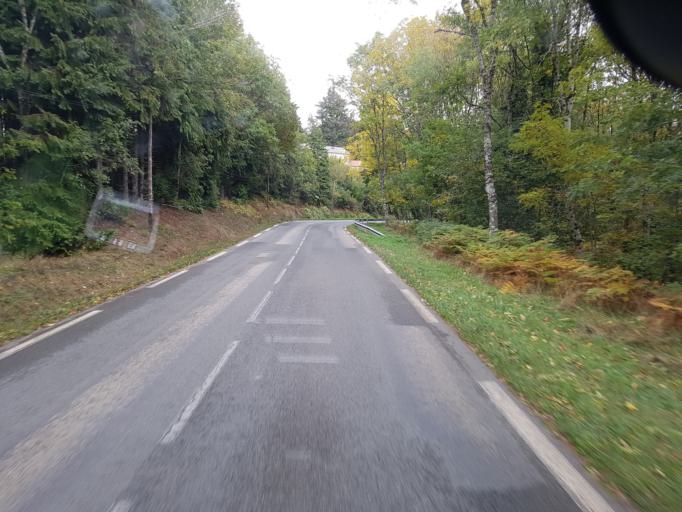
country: FR
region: Languedoc-Roussillon
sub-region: Departement de l'Aude
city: Cuxac-Cabardes
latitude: 43.4019
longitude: 2.3013
